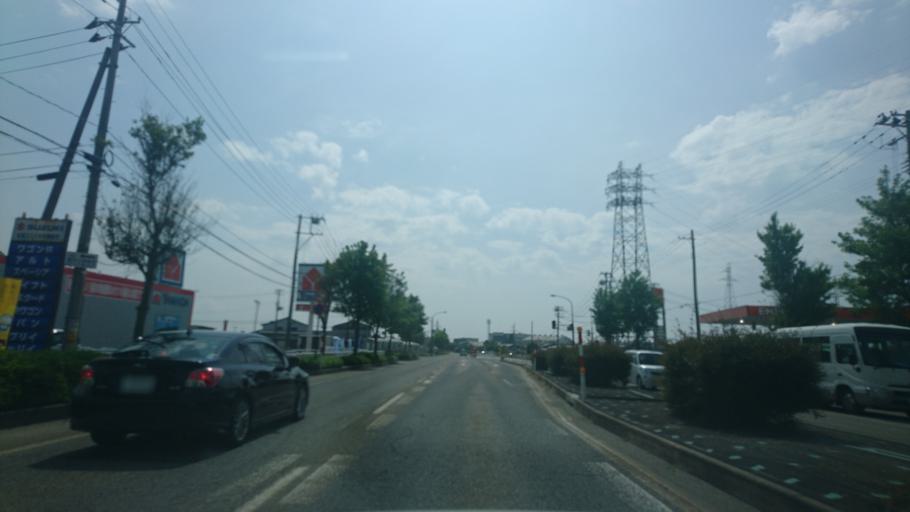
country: JP
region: Niigata
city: Shibata
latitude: 38.0462
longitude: 139.4037
